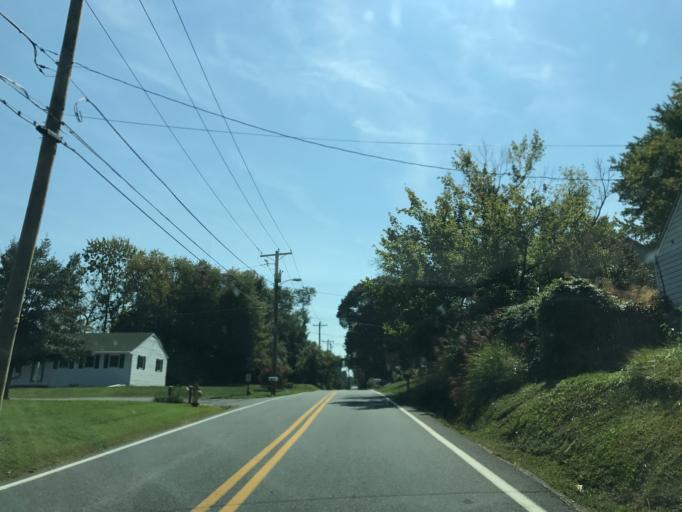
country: US
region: Maryland
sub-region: Cecil County
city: Elkton
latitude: 39.5236
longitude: -75.8154
